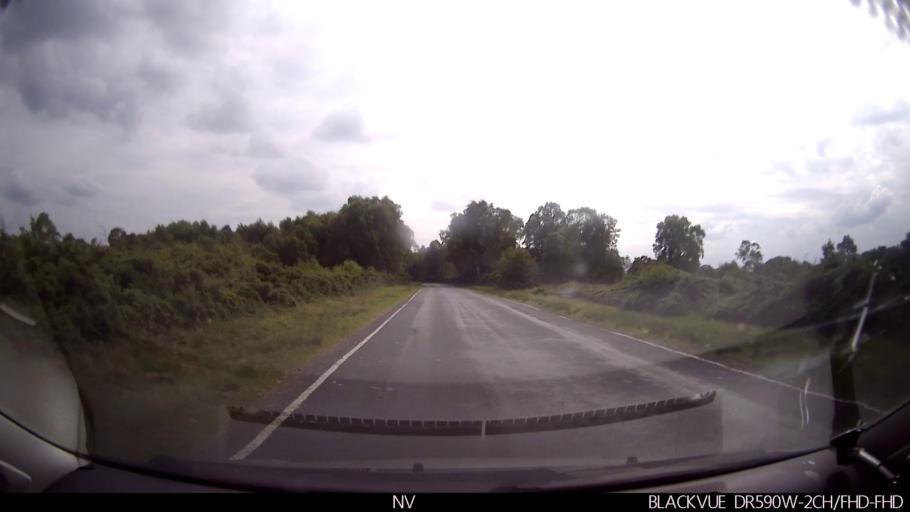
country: GB
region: England
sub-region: North Yorkshire
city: Strensall
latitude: 54.0456
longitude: -1.0078
